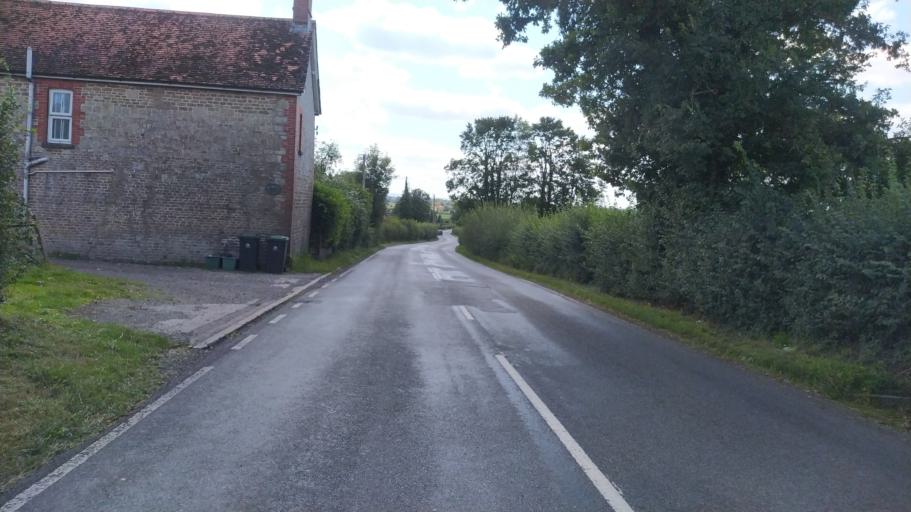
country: GB
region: England
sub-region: Wiltshire
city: Mere
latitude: 51.0698
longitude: -2.2806
